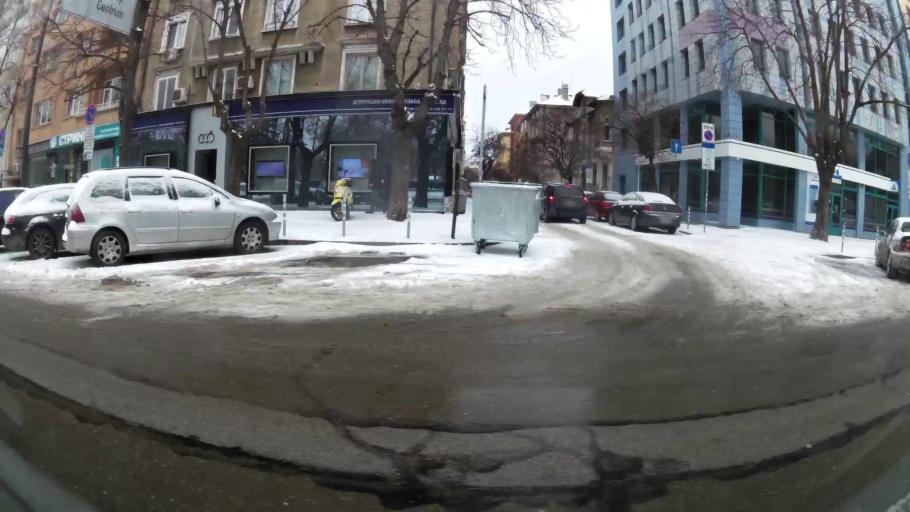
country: BG
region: Sofia-Capital
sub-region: Stolichna Obshtina
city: Sofia
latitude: 42.6877
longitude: 23.3216
